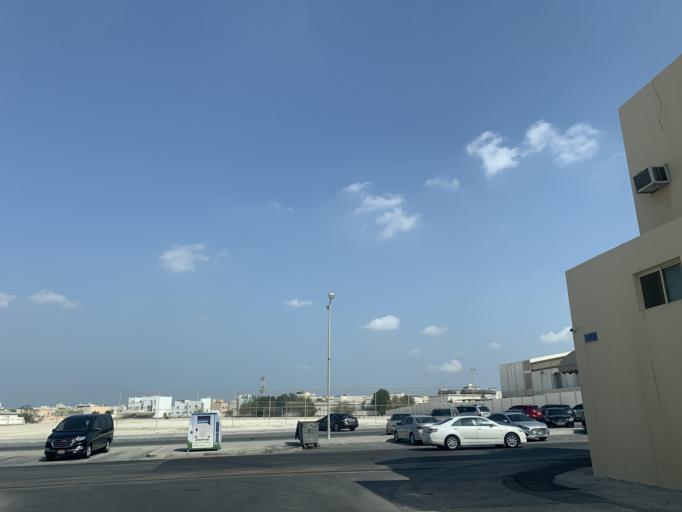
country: BH
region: Central Governorate
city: Madinat Hamad
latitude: 26.1267
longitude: 50.5027
